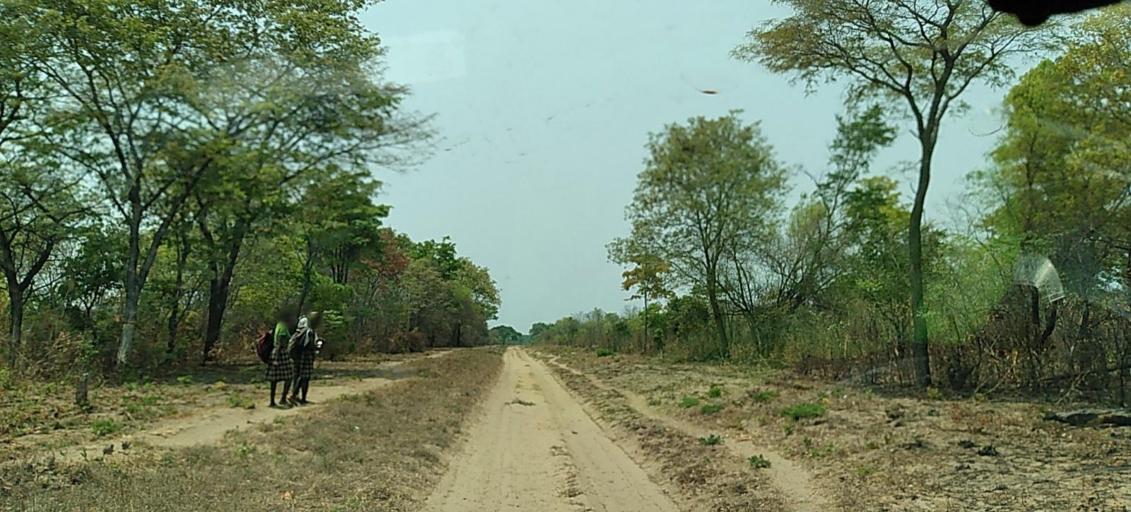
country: ZM
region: Western
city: Lukulu
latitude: -14.1504
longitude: 23.2966
